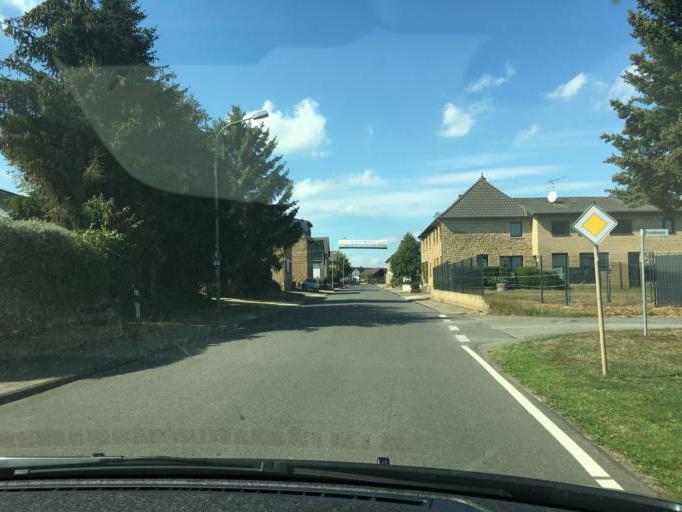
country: DE
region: North Rhine-Westphalia
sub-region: Regierungsbezirk Koln
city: Nideggen
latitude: 50.6796
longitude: 6.5261
